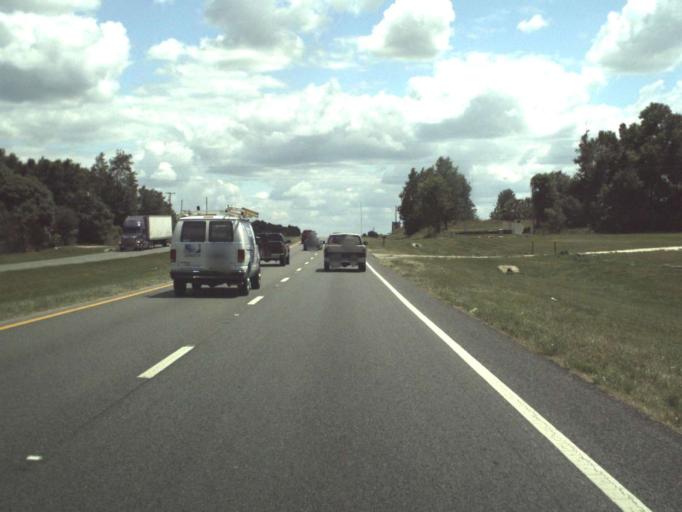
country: US
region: Florida
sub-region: Marion County
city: Ocala
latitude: 29.2573
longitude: -82.1522
